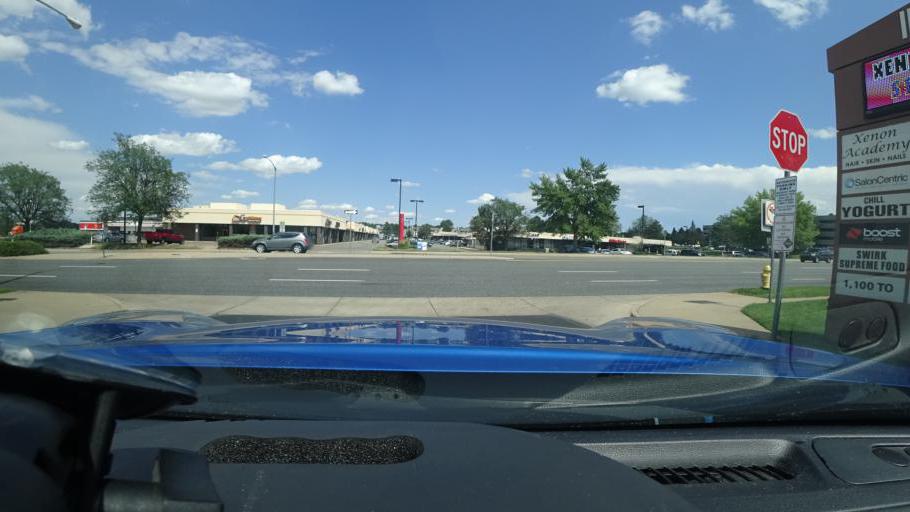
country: US
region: Colorado
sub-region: Adams County
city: Aurora
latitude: 39.6758
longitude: -104.8475
